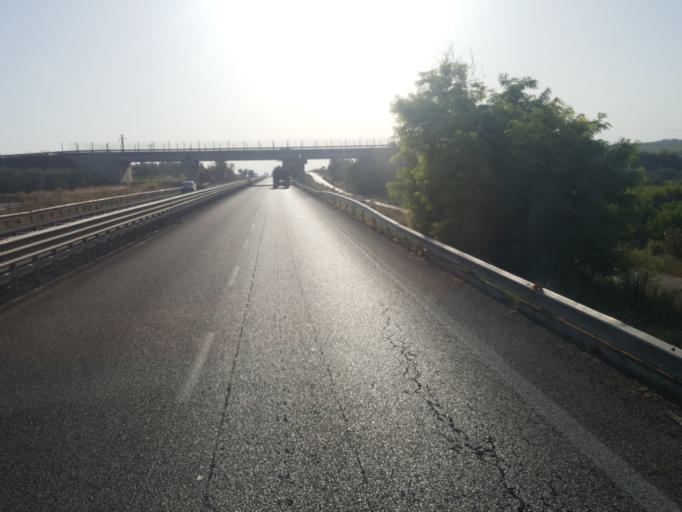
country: IT
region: Apulia
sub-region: Provincia di Barletta - Andria - Trani
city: San Ferdinando di Puglia
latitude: 41.2890
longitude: 16.0219
